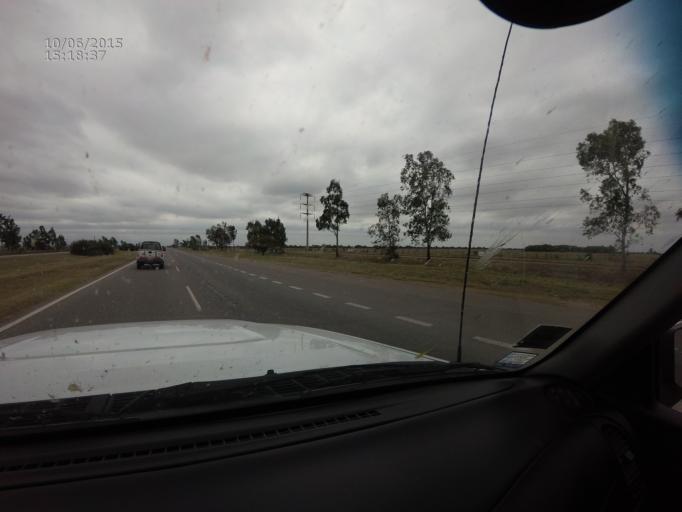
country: AR
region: Cordoba
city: Toledo
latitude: -31.5278
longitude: -63.9846
